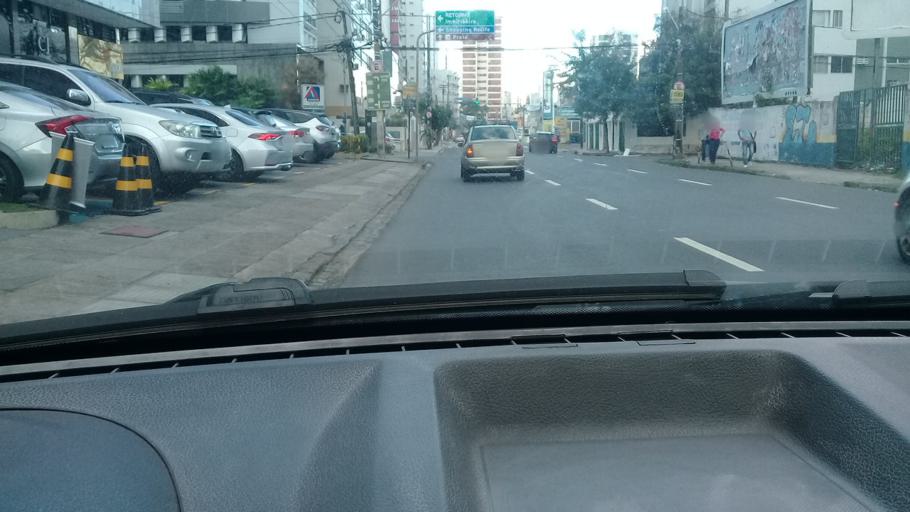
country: BR
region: Pernambuco
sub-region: Recife
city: Recife
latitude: -8.1242
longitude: -34.9066
